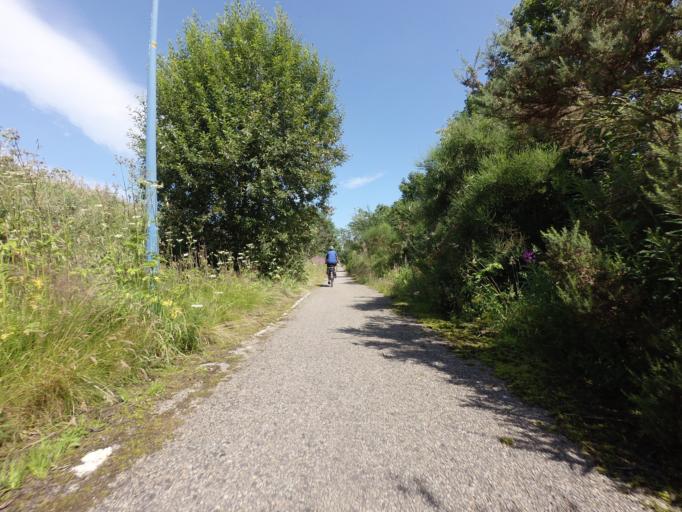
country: GB
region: Scotland
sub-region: Highland
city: Dingwall
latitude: 57.5853
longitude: -4.4304
